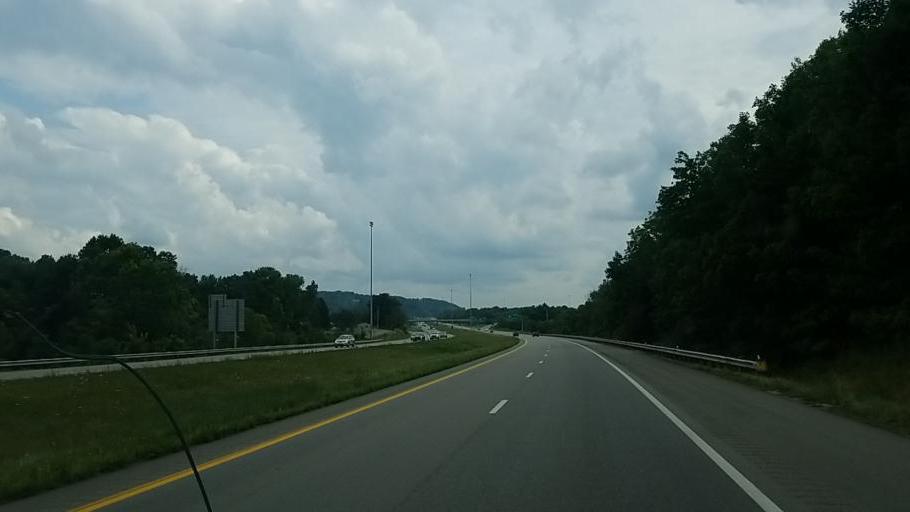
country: US
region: Ohio
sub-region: Guernsey County
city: Cambridge
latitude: 40.0355
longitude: -81.5623
